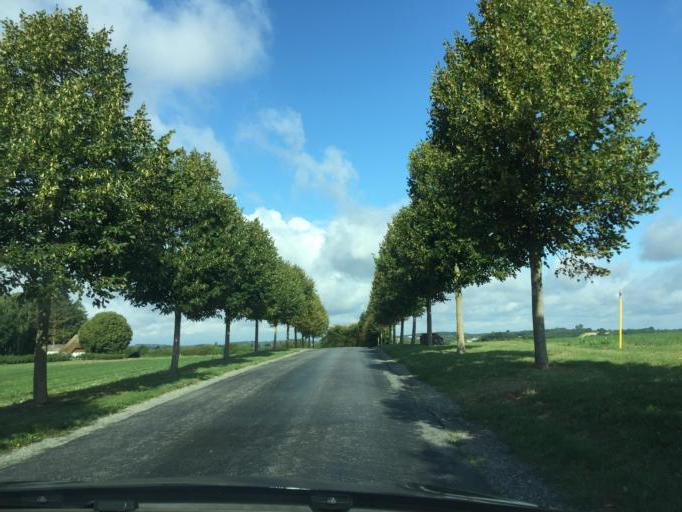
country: DK
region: South Denmark
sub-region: Faaborg-Midtfyn Kommune
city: Faaborg
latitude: 55.1958
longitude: 10.2734
